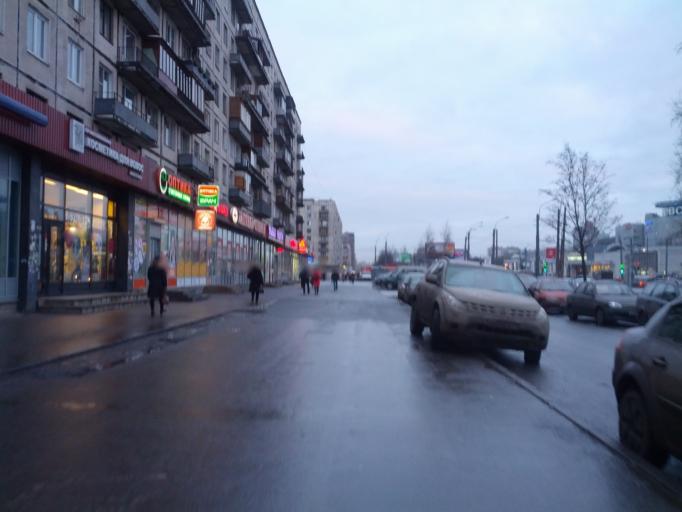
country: RU
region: Leningrad
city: Rybatskoye
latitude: 59.9050
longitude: 30.4835
